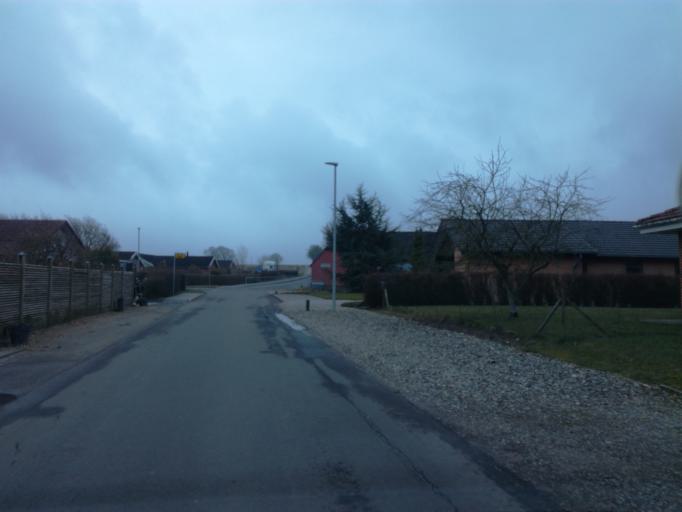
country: DK
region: South Denmark
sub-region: Vejle Kommune
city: Borkop
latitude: 55.6376
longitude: 9.5970
